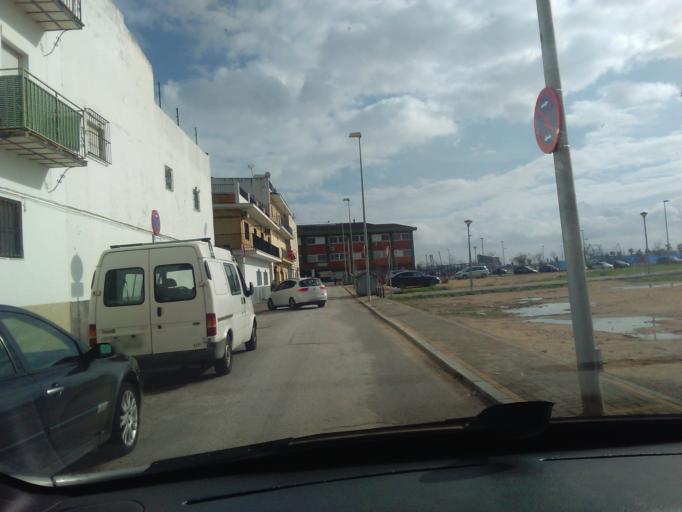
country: ES
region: Andalusia
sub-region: Provincia de Sevilla
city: Sevilla
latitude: 37.3816
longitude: -5.9128
